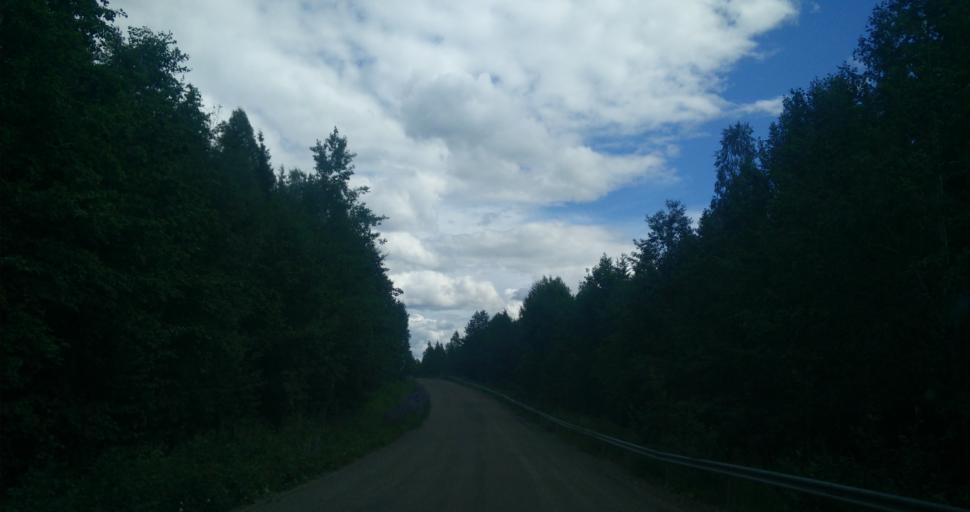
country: SE
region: Gaevleborg
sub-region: Nordanstigs Kommun
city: Bergsjoe
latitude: 62.0747
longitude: 16.7580
